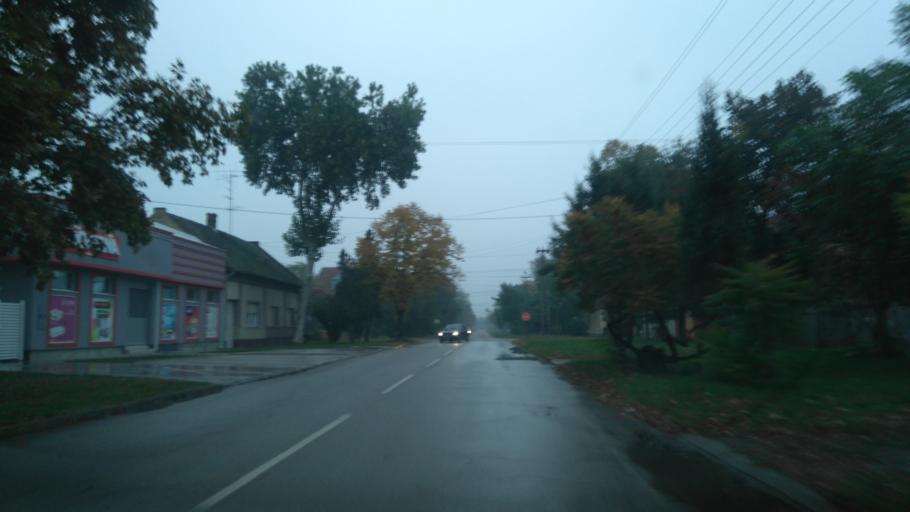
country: RS
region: Autonomna Pokrajina Vojvodina
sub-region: Juznobacki Okrug
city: Becej
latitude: 45.6202
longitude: 20.0423
